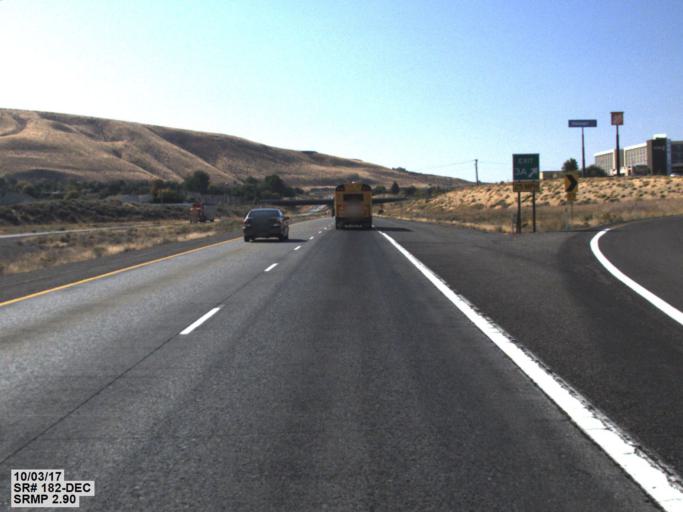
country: US
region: Washington
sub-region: Benton County
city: Richland
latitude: 46.2546
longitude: -119.3045
